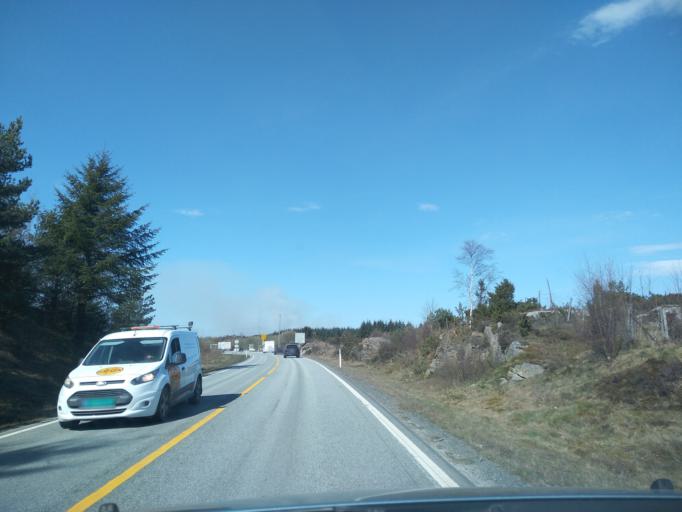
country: NO
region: Rogaland
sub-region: Tysvaer
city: Tysvaer
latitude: 59.3136
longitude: 5.4699
